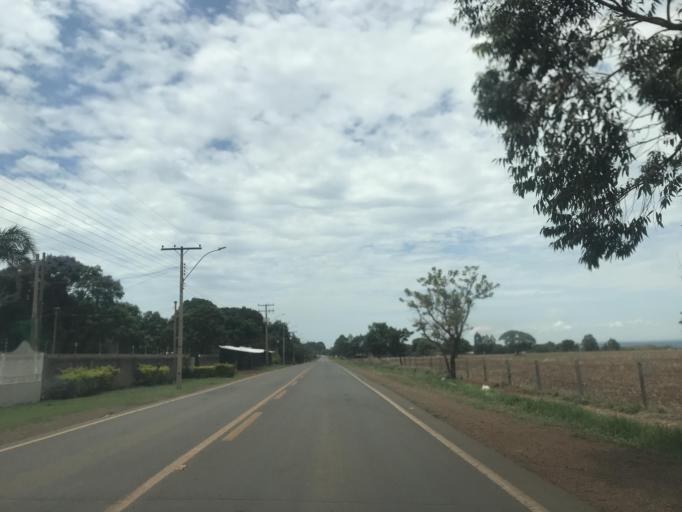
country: BR
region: Goias
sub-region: Luziania
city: Luziania
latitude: -16.3169
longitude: -48.0166
